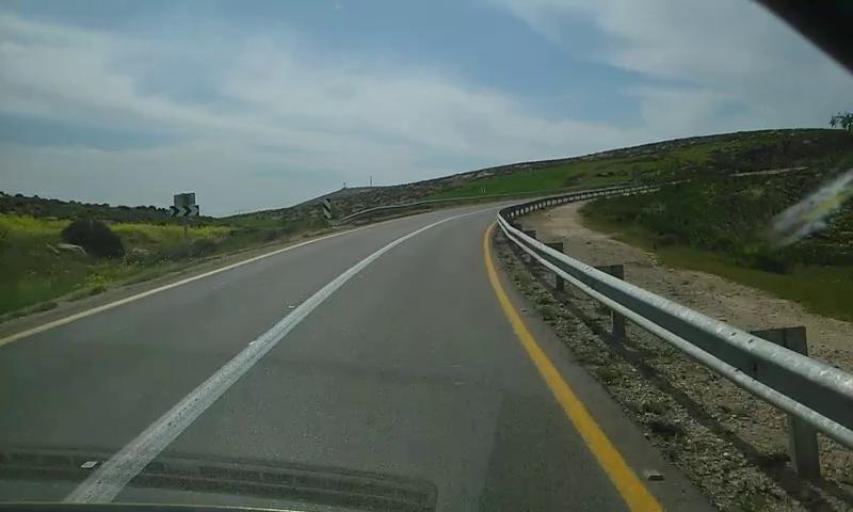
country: PS
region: West Bank
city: Az Zahiriyah
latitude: 31.3741
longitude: 35.0126
